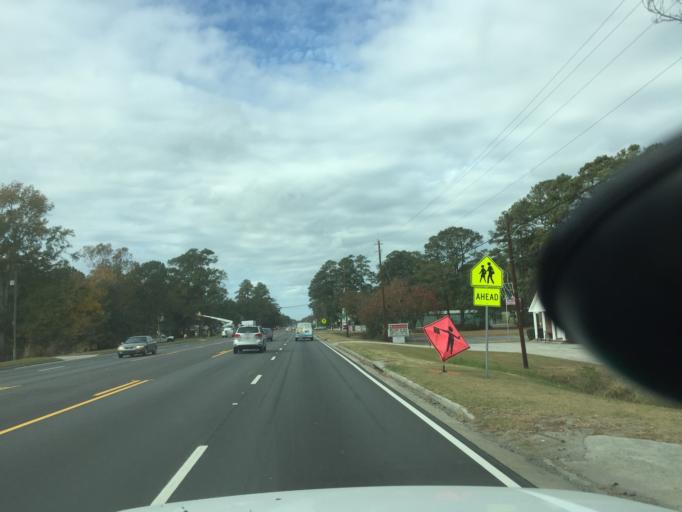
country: US
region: Georgia
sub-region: Chatham County
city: Garden City
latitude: 32.0880
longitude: -81.1754
